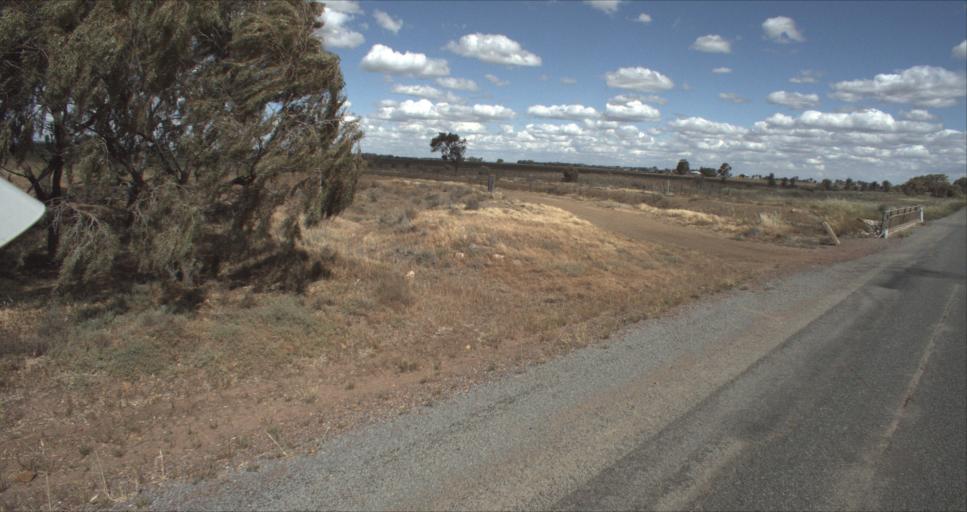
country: AU
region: New South Wales
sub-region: Leeton
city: Leeton
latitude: -34.4409
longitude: 146.2564
